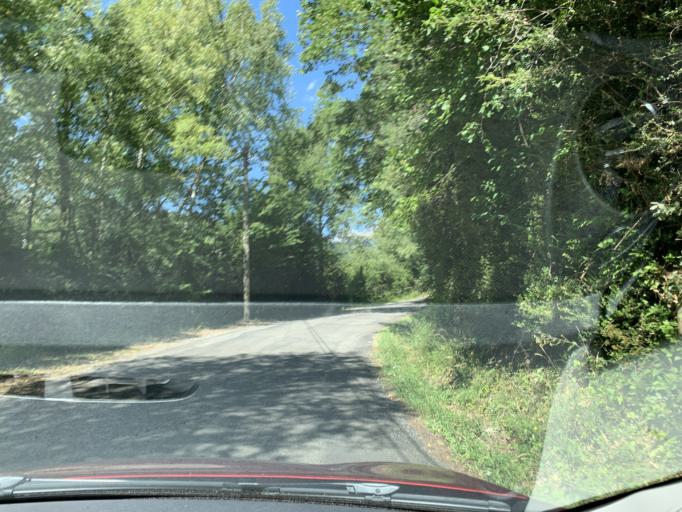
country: ES
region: Aragon
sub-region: Provincia de Huesca
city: Hoz de Jaca
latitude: 42.7006
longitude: -0.3087
